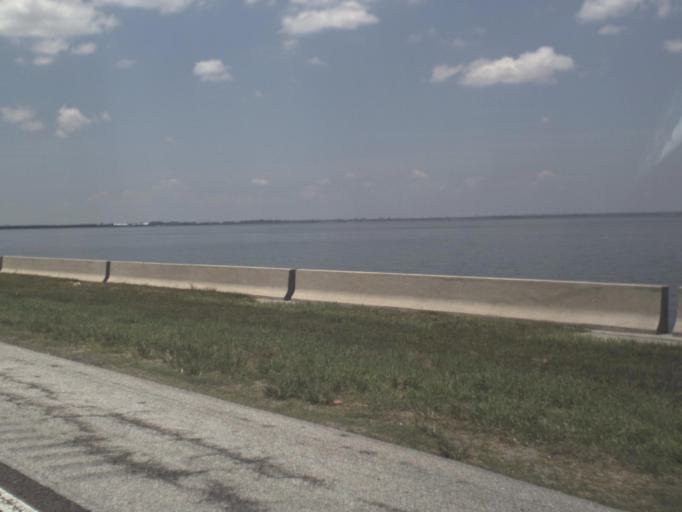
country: US
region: Florida
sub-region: Pinellas County
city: Feather Sound
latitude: 27.9167
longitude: -82.6176
